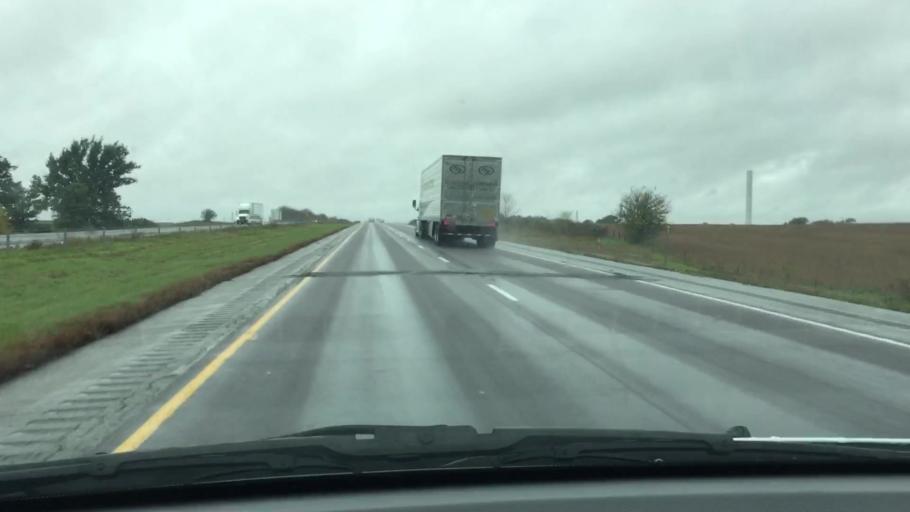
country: US
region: Iowa
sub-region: Poweshiek County
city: Montezuma
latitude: 41.6962
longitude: -92.5735
